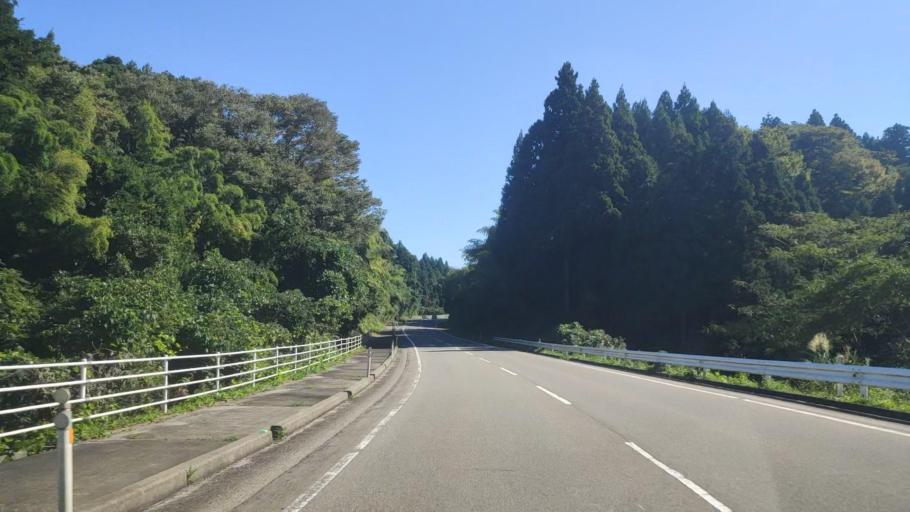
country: JP
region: Ishikawa
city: Nanao
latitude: 37.3771
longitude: 137.2335
